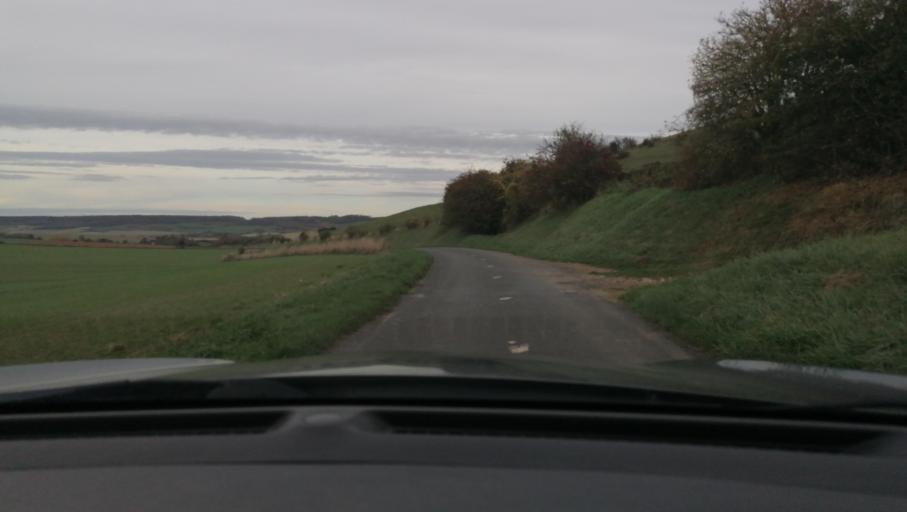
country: FR
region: Picardie
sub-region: Departement de la Somme
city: Bouttencourt
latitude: 49.8913
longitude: 1.6739
